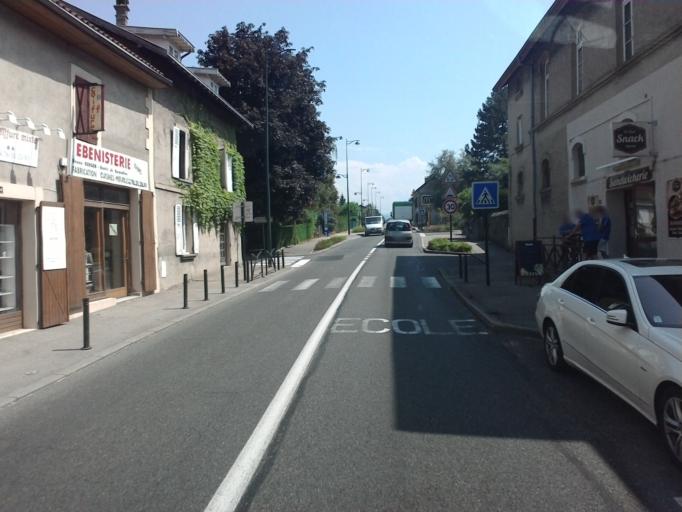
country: FR
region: Rhone-Alpes
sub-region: Departement de l'Isere
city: Chirens
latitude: 45.4140
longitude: 5.5564
